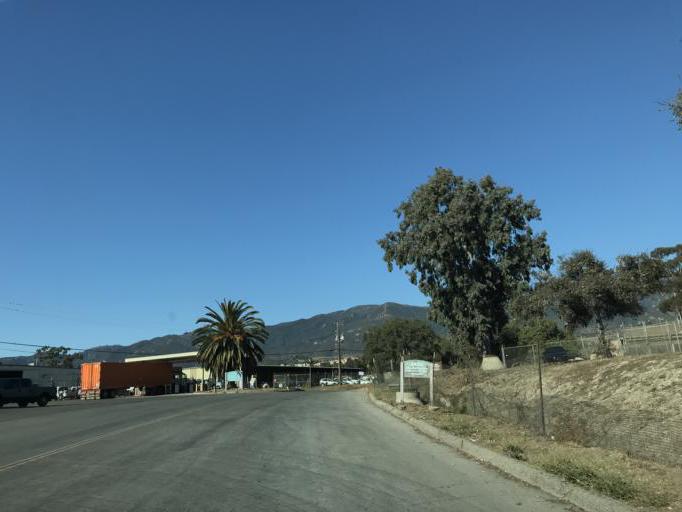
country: US
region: California
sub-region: Santa Barbara County
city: Goleta
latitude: 34.4487
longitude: -119.7735
